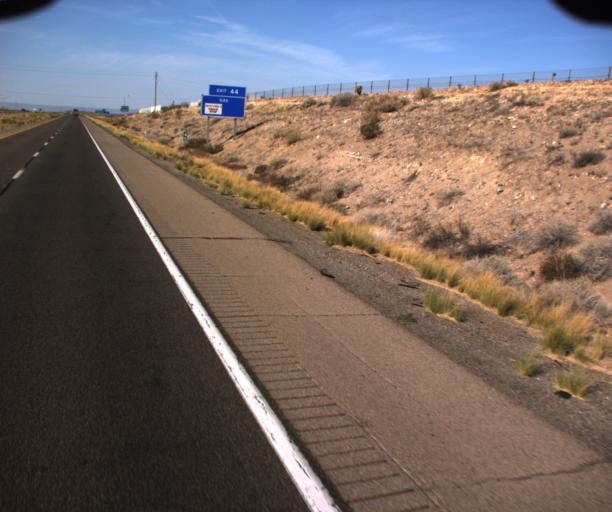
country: US
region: Arizona
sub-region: Mohave County
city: Kingman
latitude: 35.1449
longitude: -114.0964
